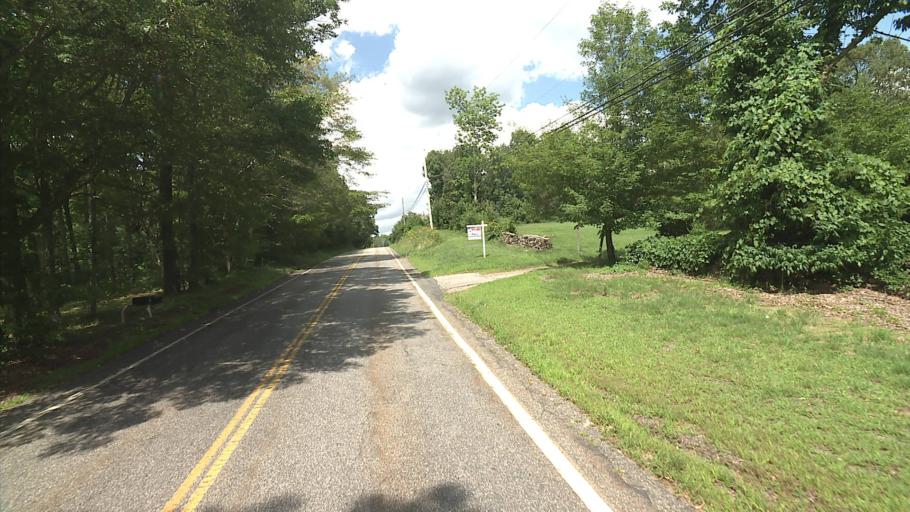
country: US
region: Connecticut
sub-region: Tolland County
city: Stafford Springs
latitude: 41.9197
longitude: -72.1919
